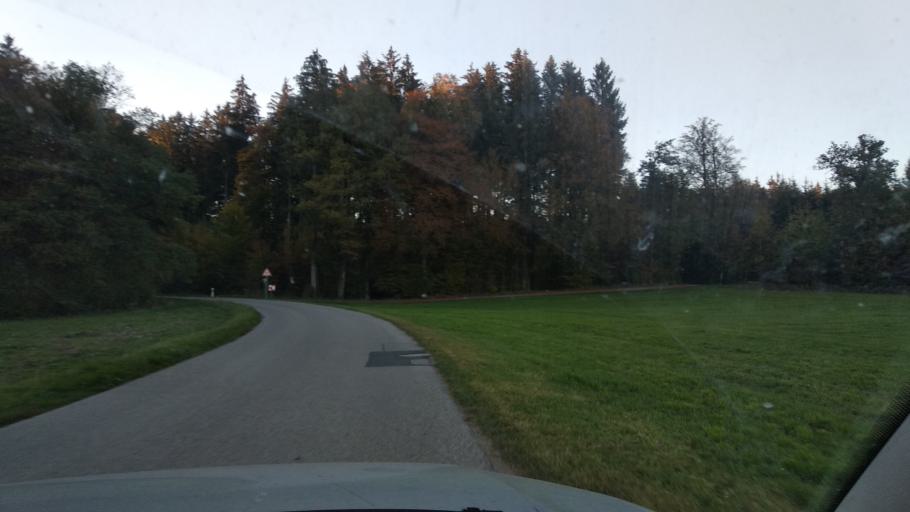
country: DE
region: Bavaria
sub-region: Upper Bavaria
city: Egmating
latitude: 47.9840
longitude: 11.8211
